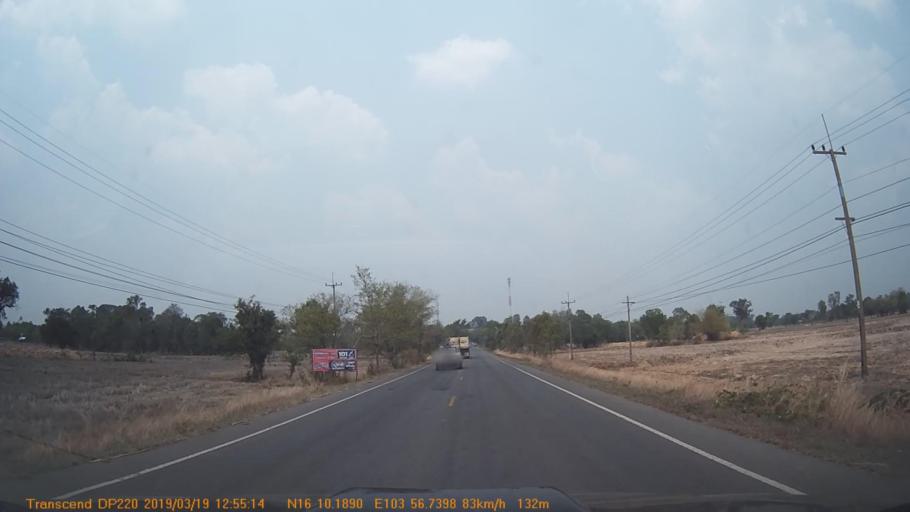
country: TH
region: Roi Et
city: Waeng
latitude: 16.1701
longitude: 103.9457
